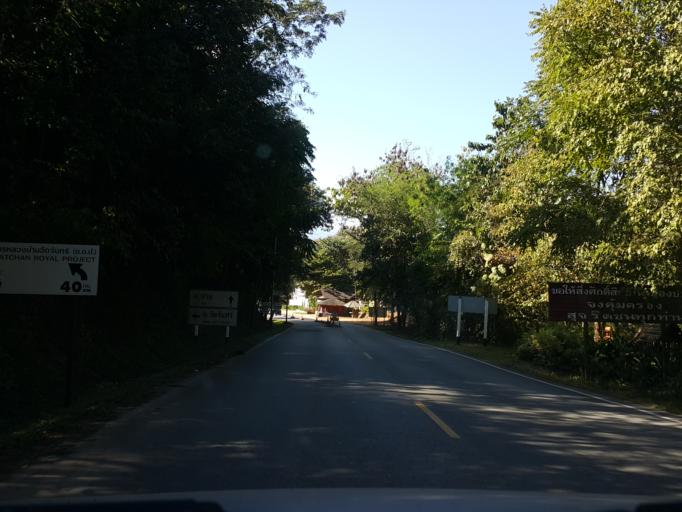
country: TH
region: Mae Hong Son
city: Mae Hi
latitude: 19.2848
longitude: 98.4845
